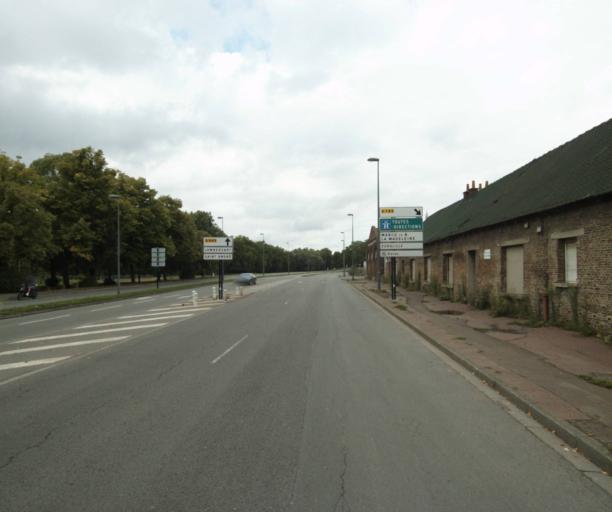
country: FR
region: Nord-Pas-de-Calais
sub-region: Departement du Nord
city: Lille
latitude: 50.6454
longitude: 3.0507
